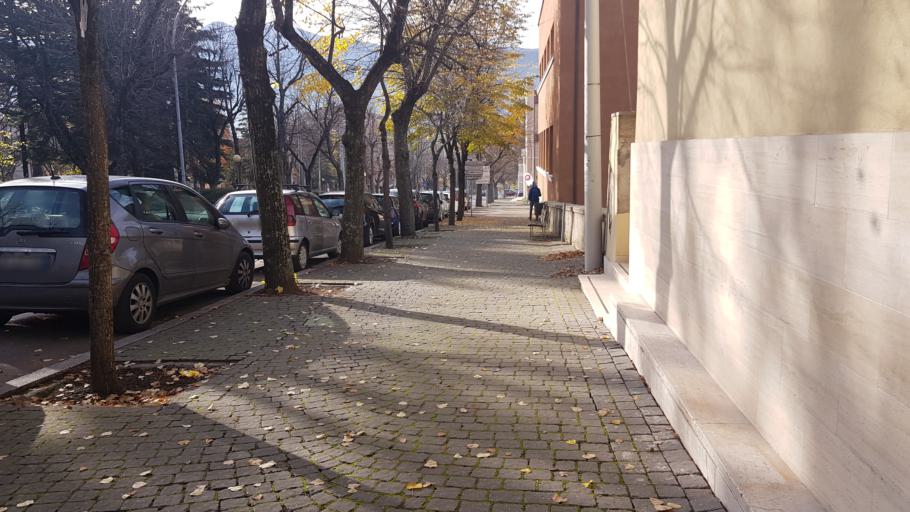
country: IT
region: Abruzzo
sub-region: Provincia dell' Aquila
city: L'Aquila
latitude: 42.3451
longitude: 13.3969
